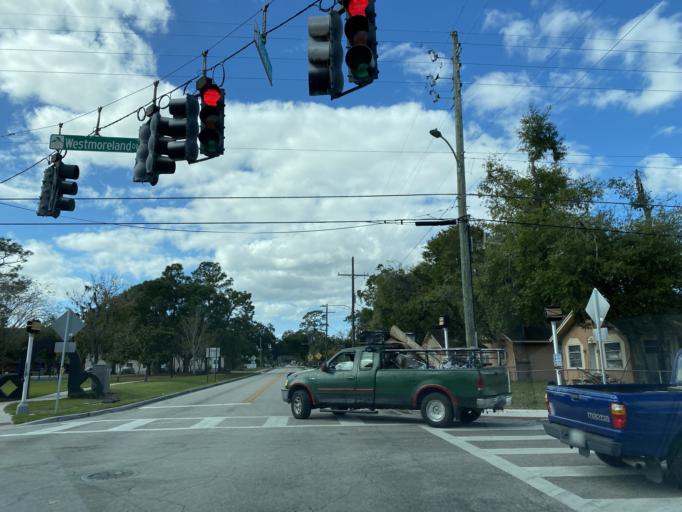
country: US
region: Florida
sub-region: Orange County
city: Orlando
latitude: 28.5201
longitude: -81.3928
